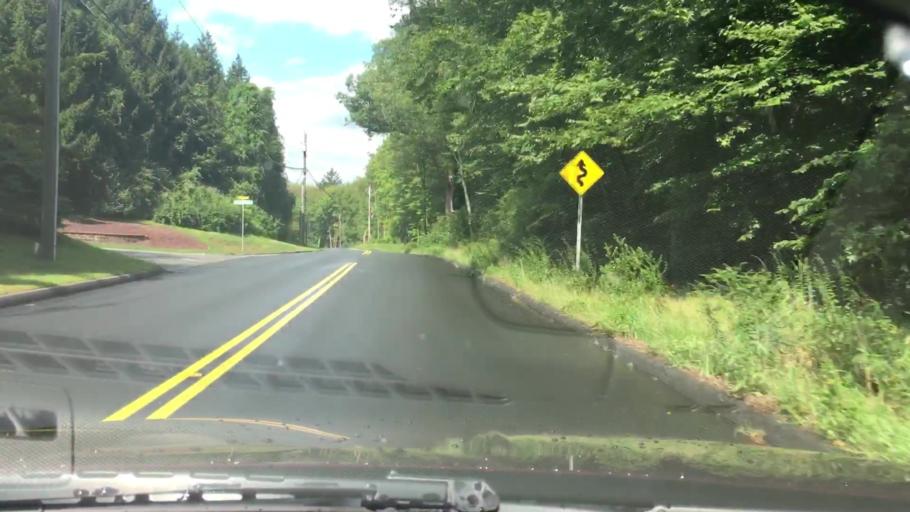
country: US
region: Connecticut
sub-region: Hartford County
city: Manchester
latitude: 41.7269
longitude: -72.5359
